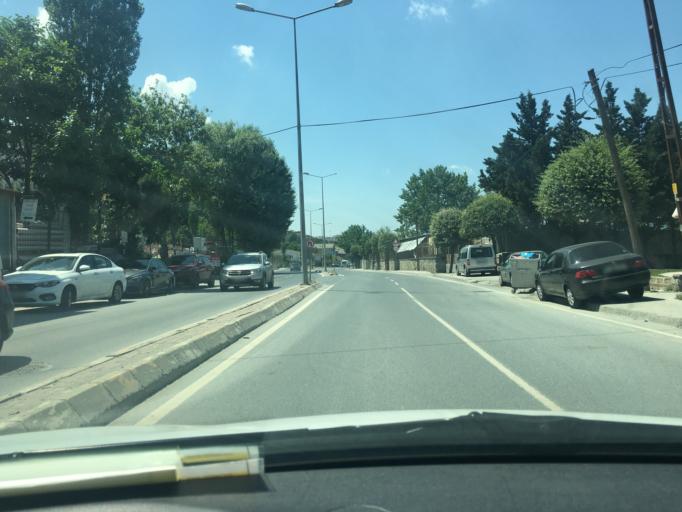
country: TR
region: Istanbul
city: Sisli
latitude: 41.0871
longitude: 28.9366
